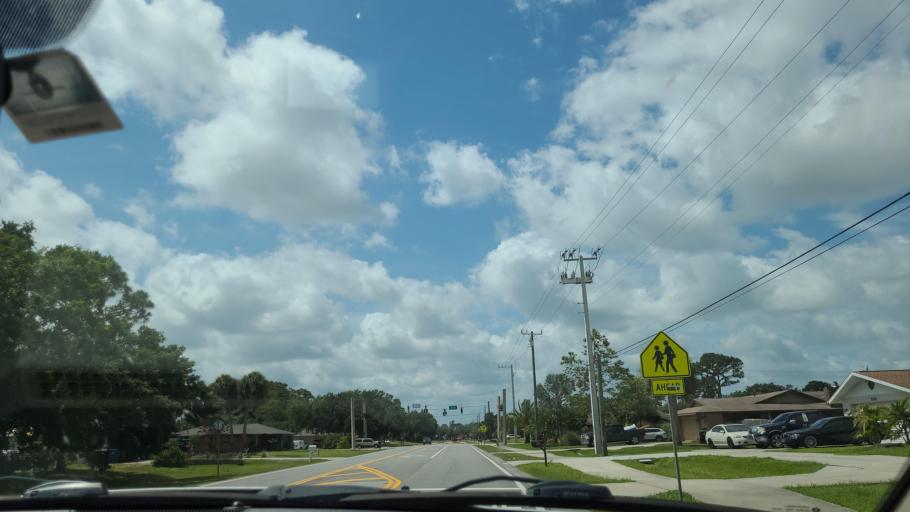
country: US
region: Florida
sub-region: Brevard County
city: West Melbourne
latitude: 28.0260
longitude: -80.6604
